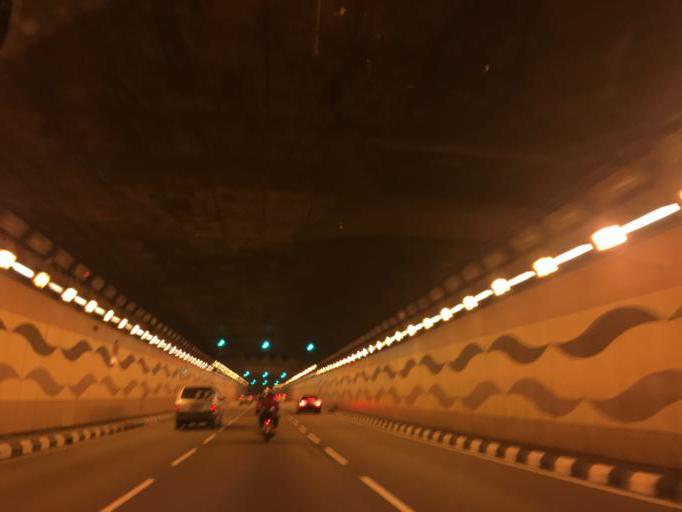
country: MY
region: Kuala Lumpur
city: Kuala Lumpur
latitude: 3.1463
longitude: 101.7223
